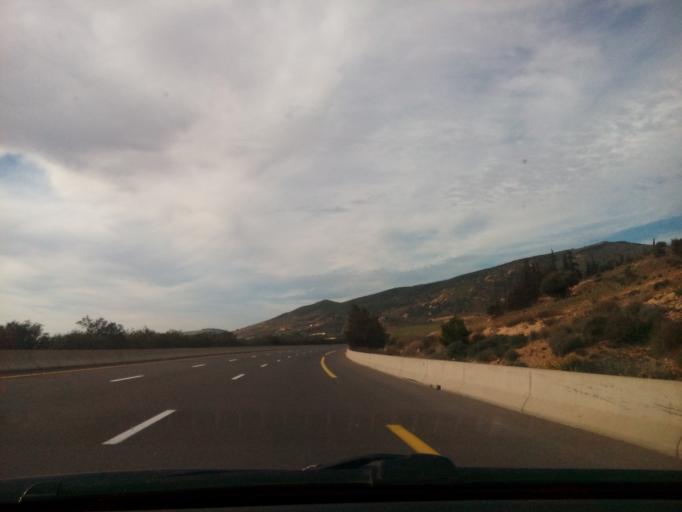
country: DZ
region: Sidi Bel Abbes
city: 'Ain el Berd
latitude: 35.3879
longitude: -0.4910
